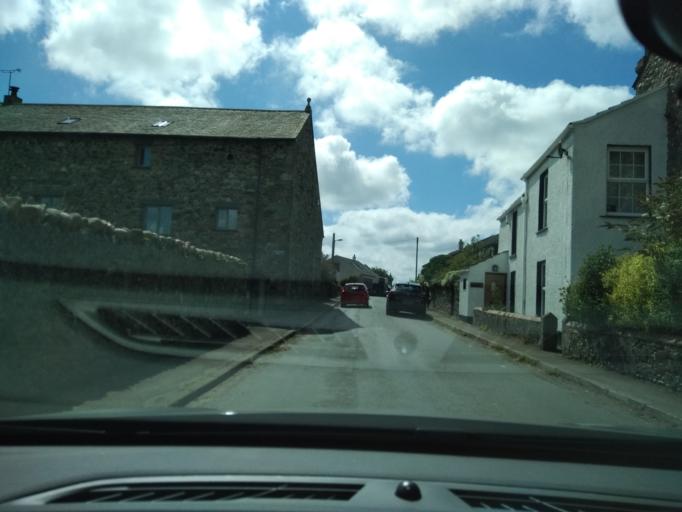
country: GB
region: England
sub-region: Cumbria
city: Millom
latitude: 54.2248
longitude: -3.3360
